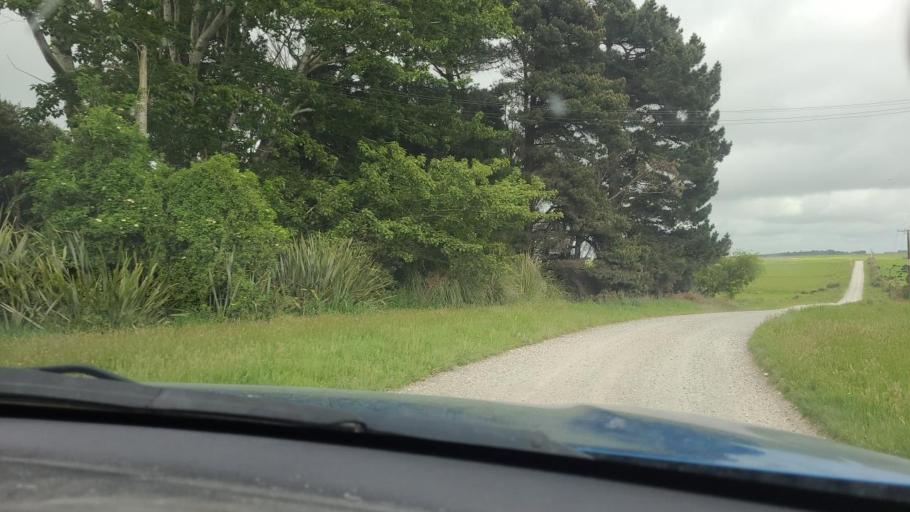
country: NZ
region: Southland
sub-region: Invercargill City
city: Invercargill
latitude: -46.4404
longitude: 168.5914
